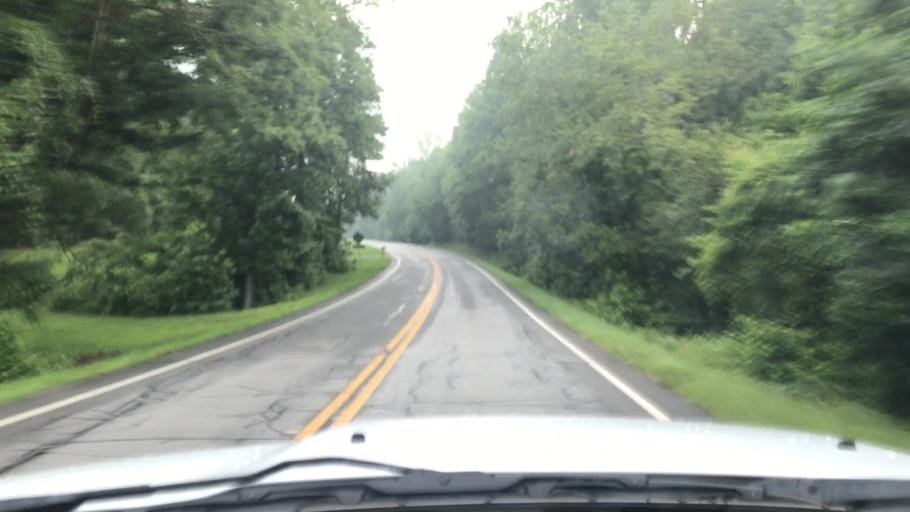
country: US
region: Georgia
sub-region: Fannin County
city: Blue Ridge
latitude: 34.9613
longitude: -84.2243
